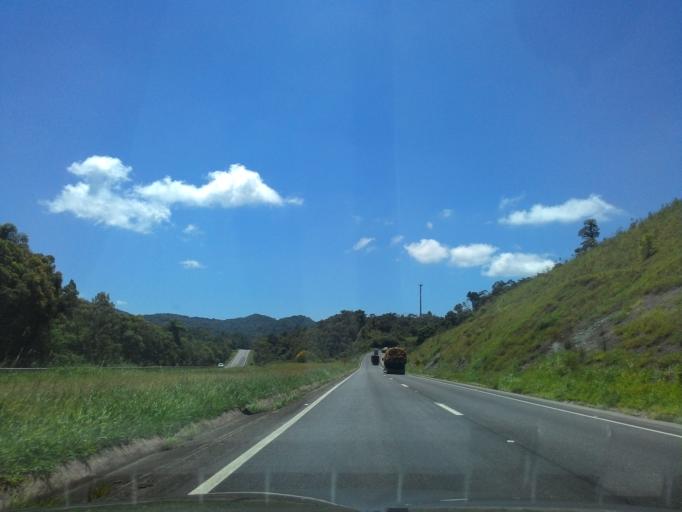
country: BR
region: Parana
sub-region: Antonina
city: Antonina
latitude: -25.0888
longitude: -48.6453
